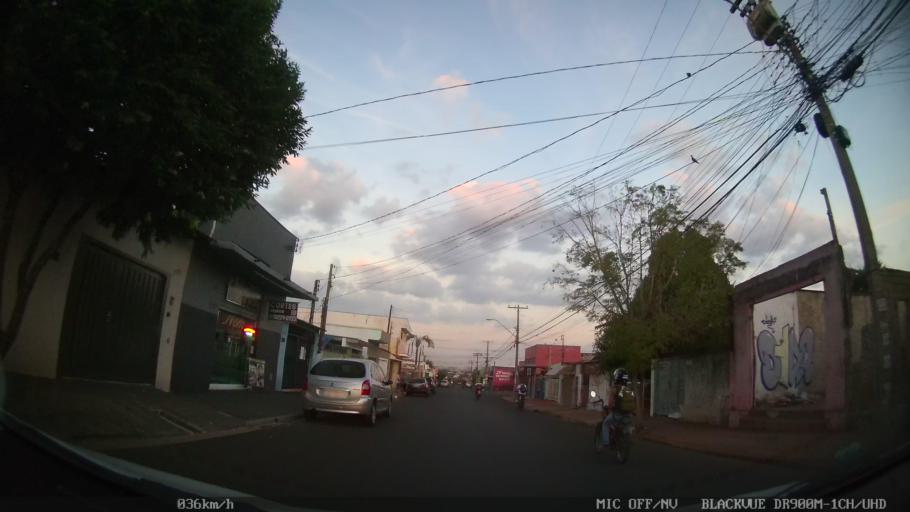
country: BR
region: Sao Paulo
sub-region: Ribeirao Preto
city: Ribeirao Preto
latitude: -21.1483
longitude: -47.8159
